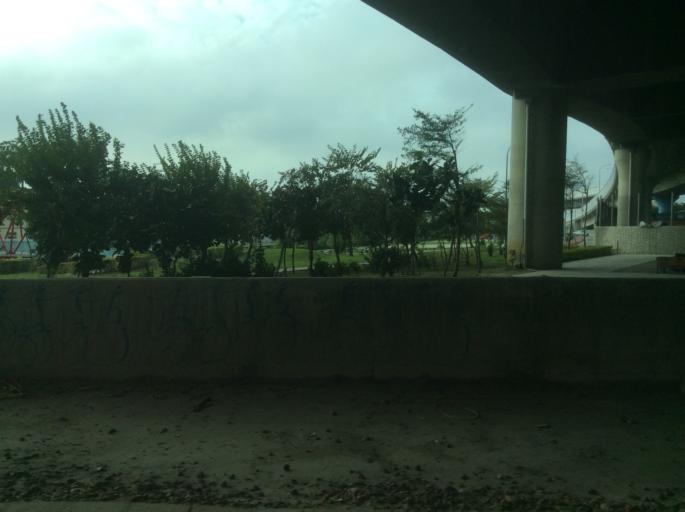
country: TW
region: Taiwan
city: Fengyuan
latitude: 24.2679
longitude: 120.5707
